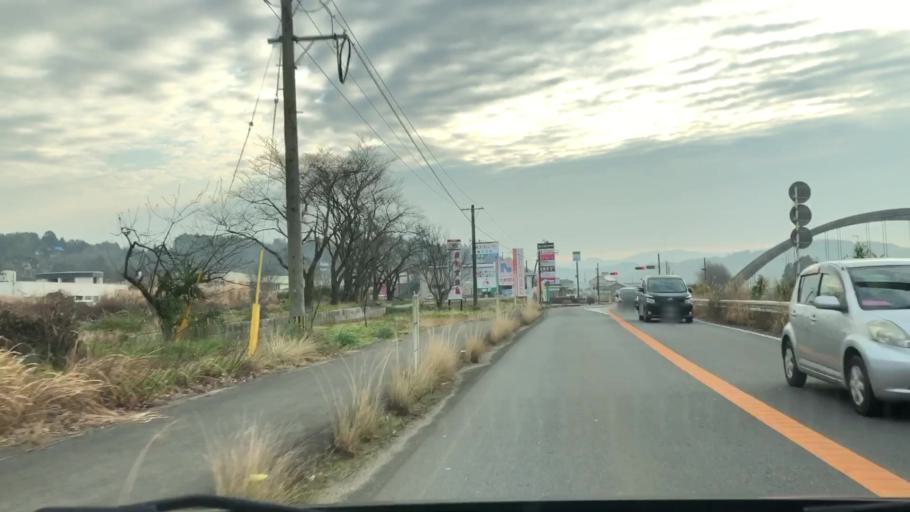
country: JP
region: Oita
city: Takedamachi
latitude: 32.9695
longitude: 131.4726
